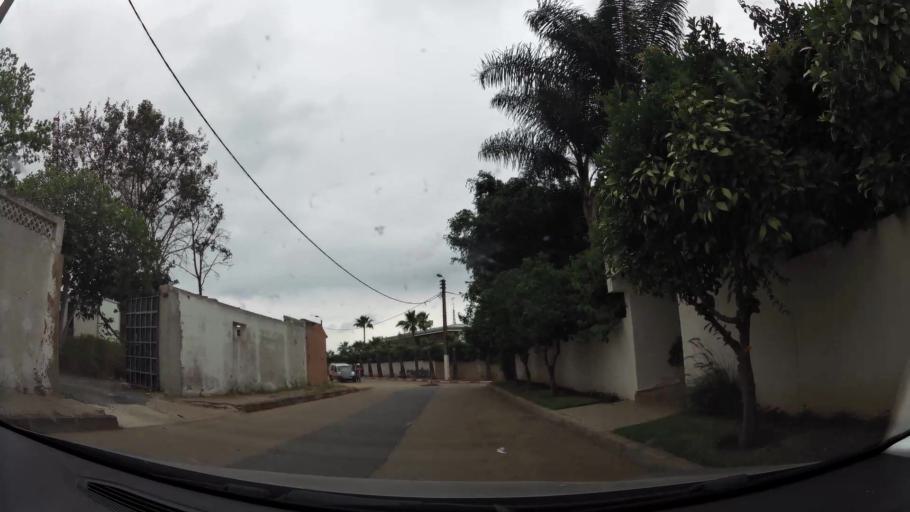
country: MA
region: Rabat-Sale-Zemmour-Zaer
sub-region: Rabat
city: Rabat
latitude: 33.9588
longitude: -6.8131
